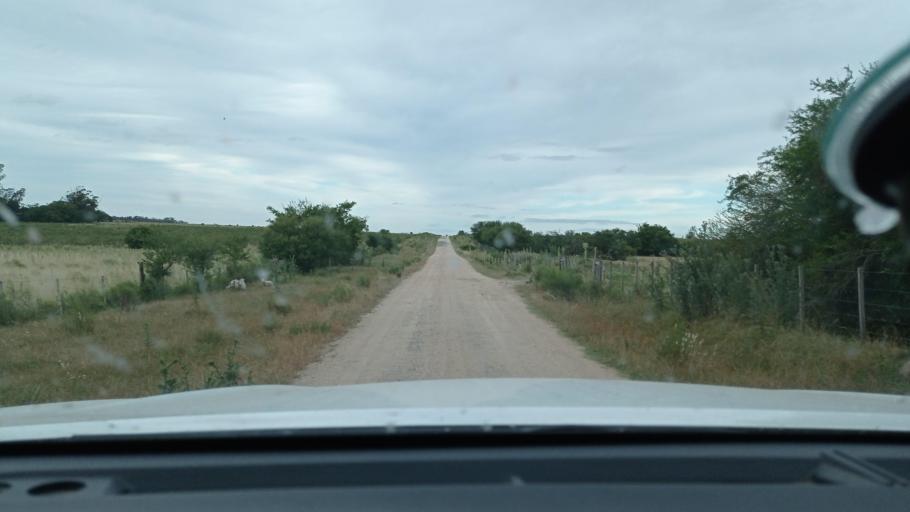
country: UY
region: Florida
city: Casupa
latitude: -34.1466
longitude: -55.7920
